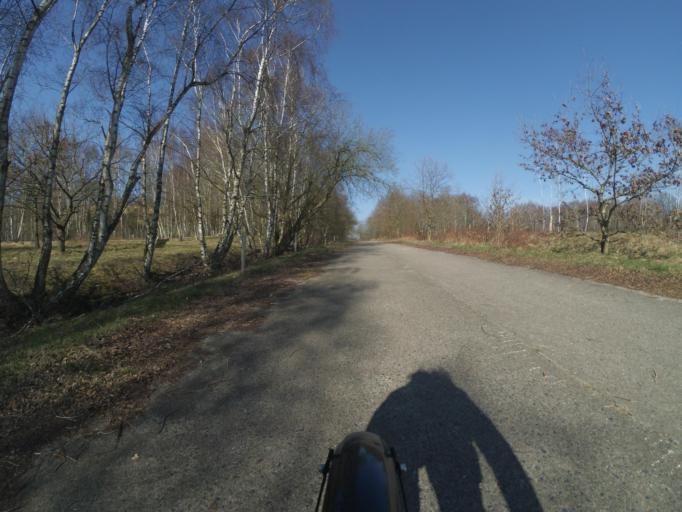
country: DE
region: Schleswig-Holstein
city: Stapelfeld
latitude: 53.6265
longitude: 10.1971
